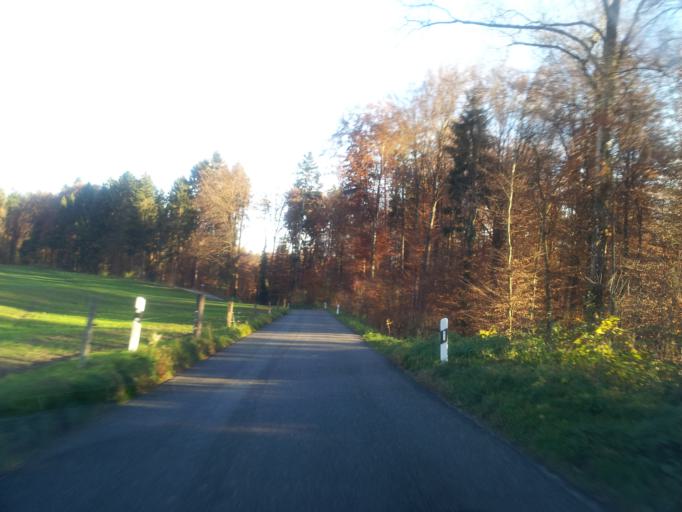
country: CH
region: Zurich
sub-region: Bezirk Dielsdorf
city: Daenikon
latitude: 47.4359
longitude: 8.3878
